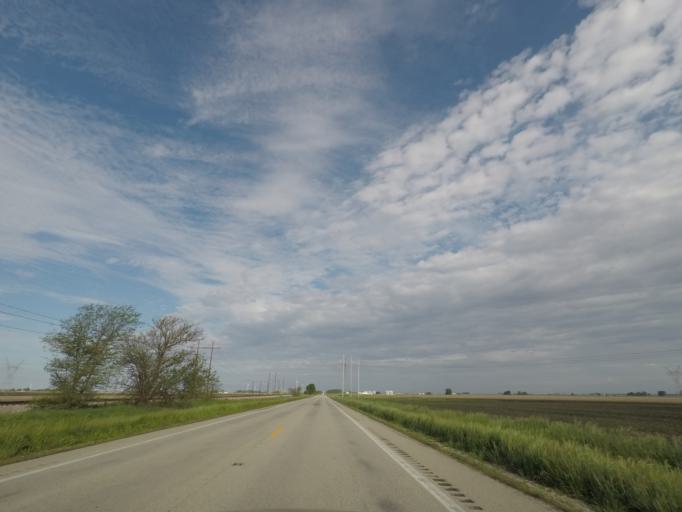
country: US
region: Illinois
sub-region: Logan County
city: Mount Pulaski
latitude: 39.9739
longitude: -89.1873
